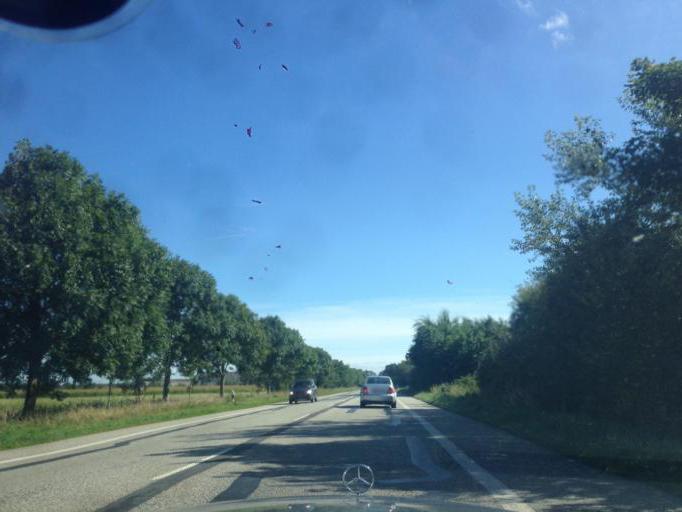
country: DE
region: Schleswig-Holstein
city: Stedesand
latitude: 54.7426
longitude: 8.9246
